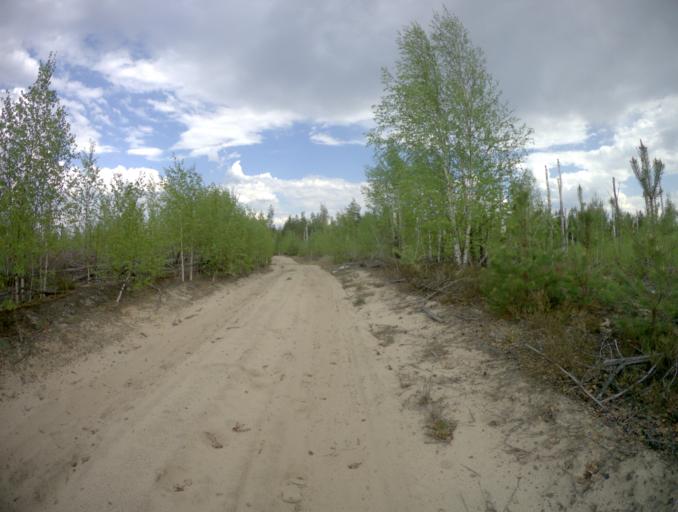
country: RU
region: Ivanovo
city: Talitsy
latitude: 56.4440
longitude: 42.2602
